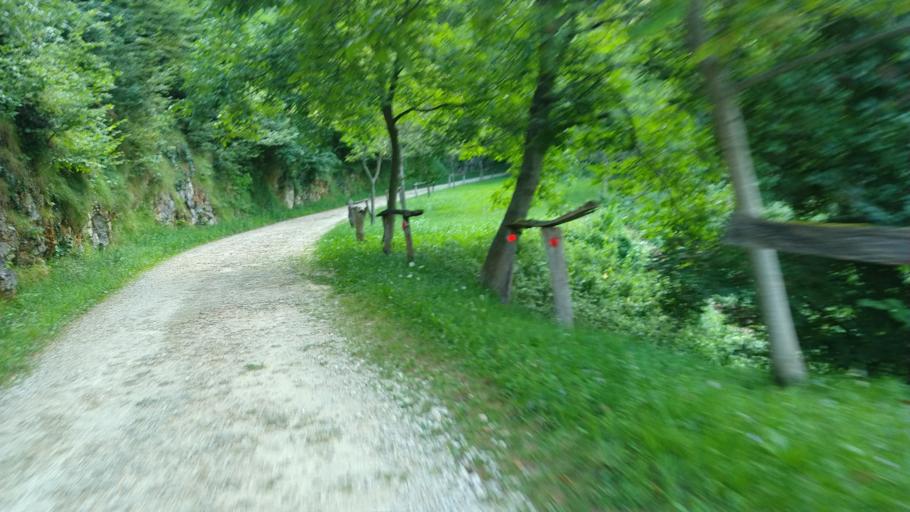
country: IT
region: Veneto
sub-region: Provincia di Vicenza
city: Campolongo sul Brenta
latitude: 45.8258
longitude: 11.6882
